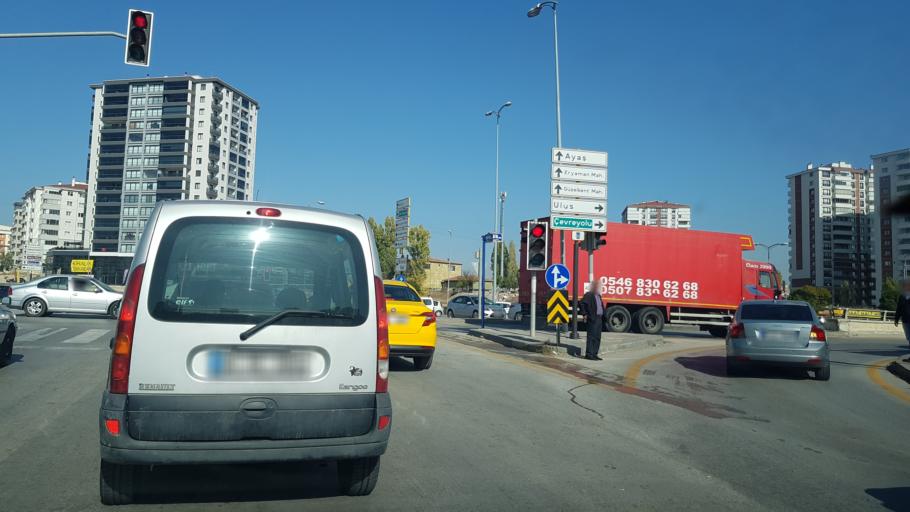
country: TR
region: Ankara
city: Etimesgut
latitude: 39.9700
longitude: 32.6087
